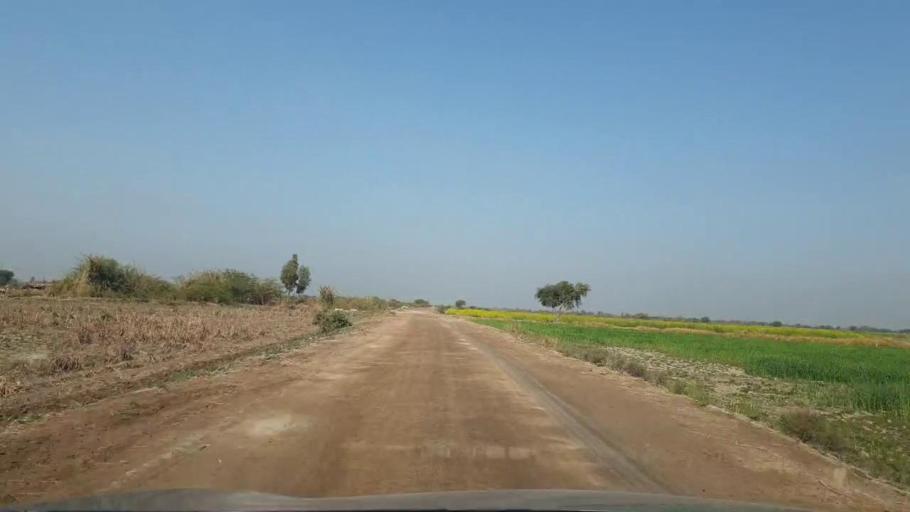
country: PK
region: Sindh
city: Berani
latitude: 25.7084
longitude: 68.8628
